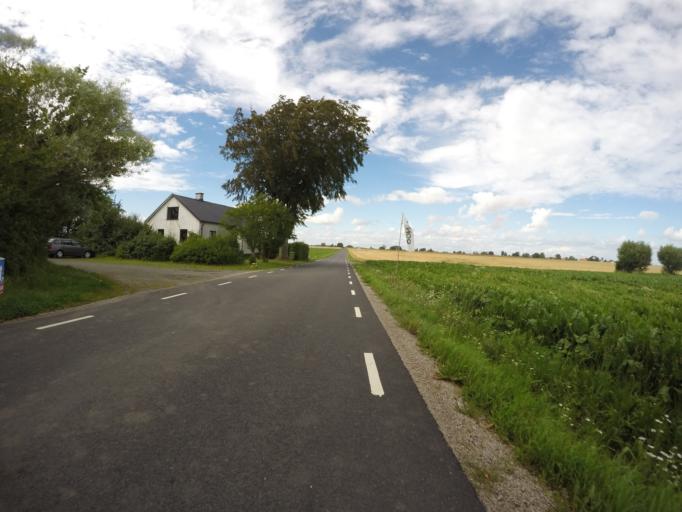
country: SE
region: Skane
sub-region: Ystads Kommun
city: Kopingebro
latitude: 55.4182
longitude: 14.1489
